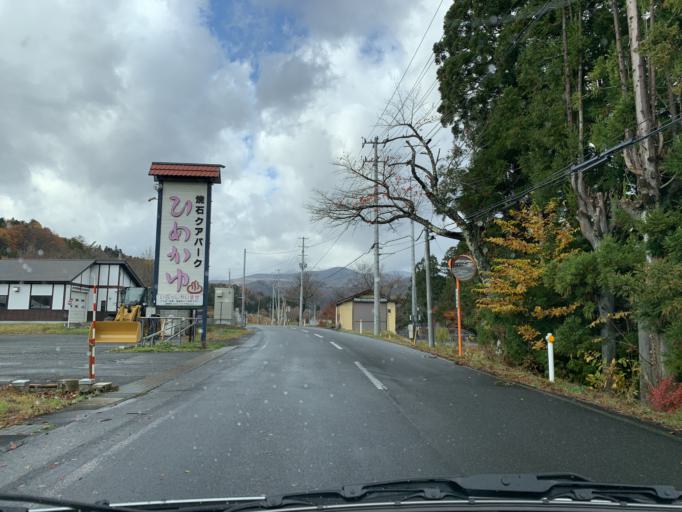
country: JP
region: Iwate
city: Mizusawa
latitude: 39.1167
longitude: 140.9442
